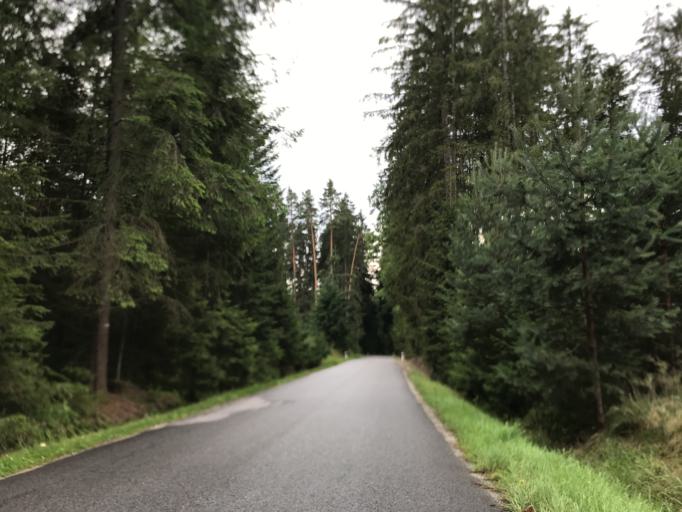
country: CZ
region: Jihocesky
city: Suchdol nad Luznici
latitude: 48.9376
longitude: 14.8522
